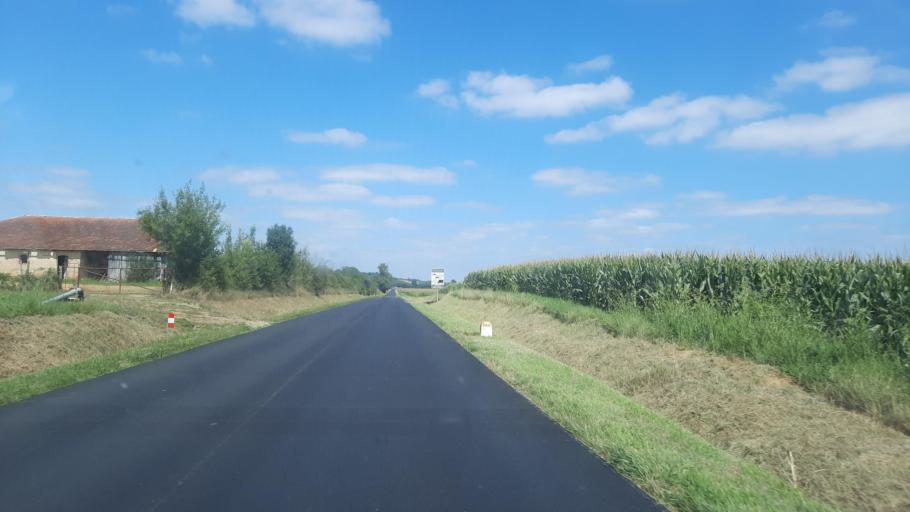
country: FR
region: Midi-Pyrenees
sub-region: Departement du Gers
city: Lombez
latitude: 43.4510
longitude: 0.8734
